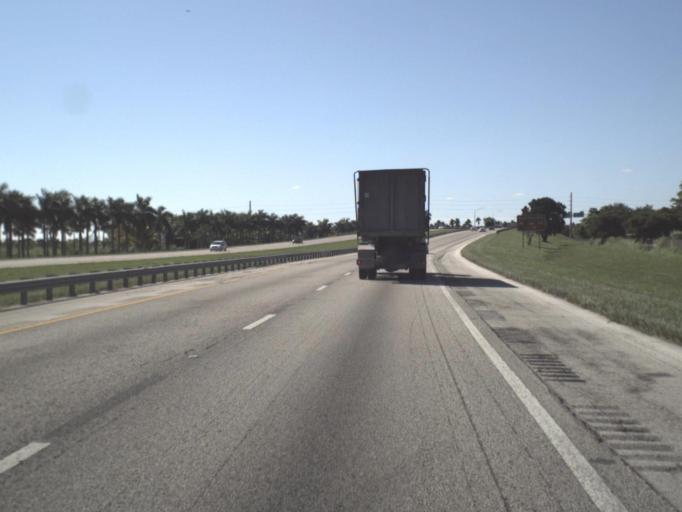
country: US
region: Florida
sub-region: Miami-Dade County
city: Goulds
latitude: 25.5414
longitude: -80.3638
